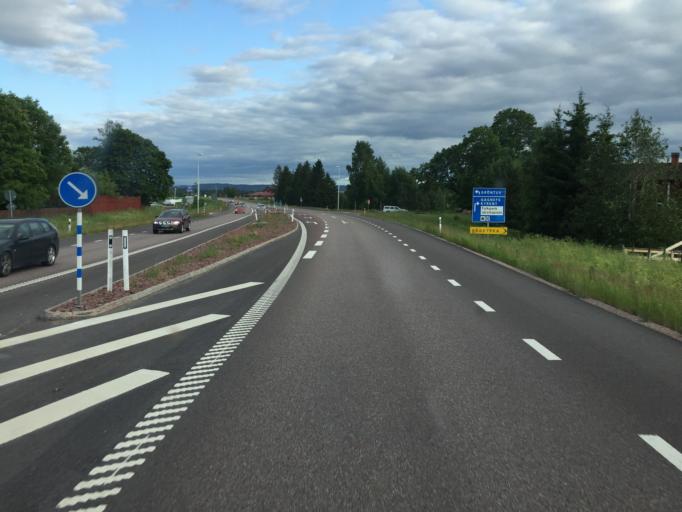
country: SE
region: Dalarna
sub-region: Gagnefs Kommun
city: Gagnef
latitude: 60.5914
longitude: 15.0848
